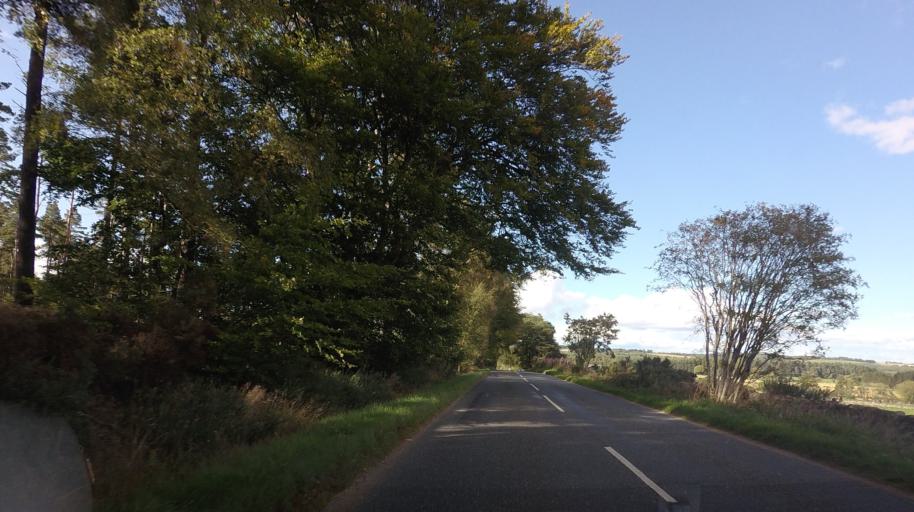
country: GB
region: Scotland
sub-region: Aberdeenshire
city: Banchory
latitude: 57.1235
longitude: -2.4259
